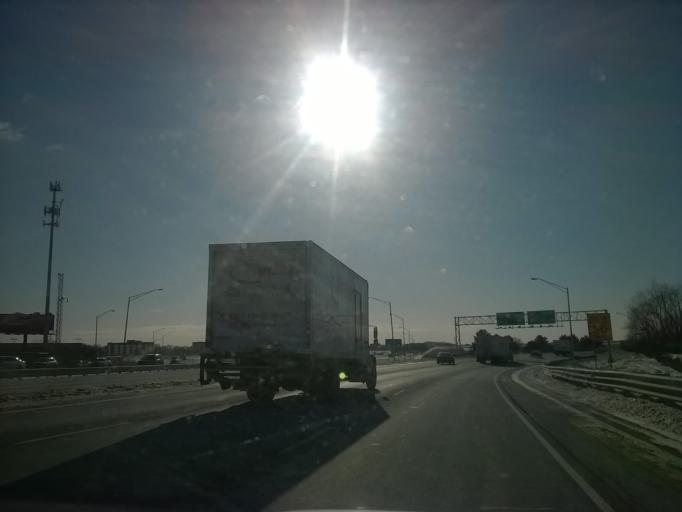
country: US
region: Indiana
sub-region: Marion County
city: Lawrence
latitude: 39.8992
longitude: -86.0510
